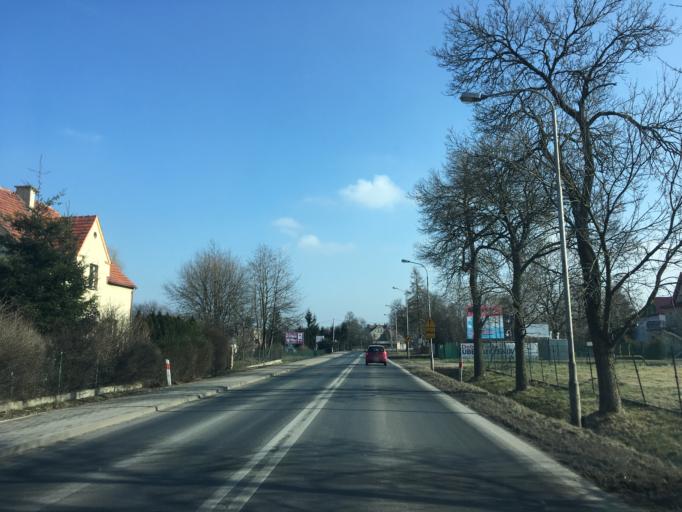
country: PL
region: Lower Silesian Voivodeship
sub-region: Powiat boleslawiecki
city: Boleslawiec
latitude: 51.2613
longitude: 15.6084
